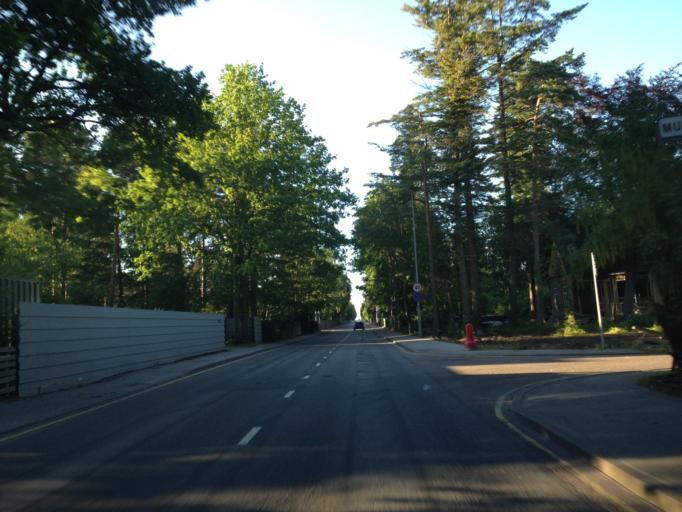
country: EE
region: Harju
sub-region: Saue vald
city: Laagri
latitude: 59.3744
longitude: 24.6341
